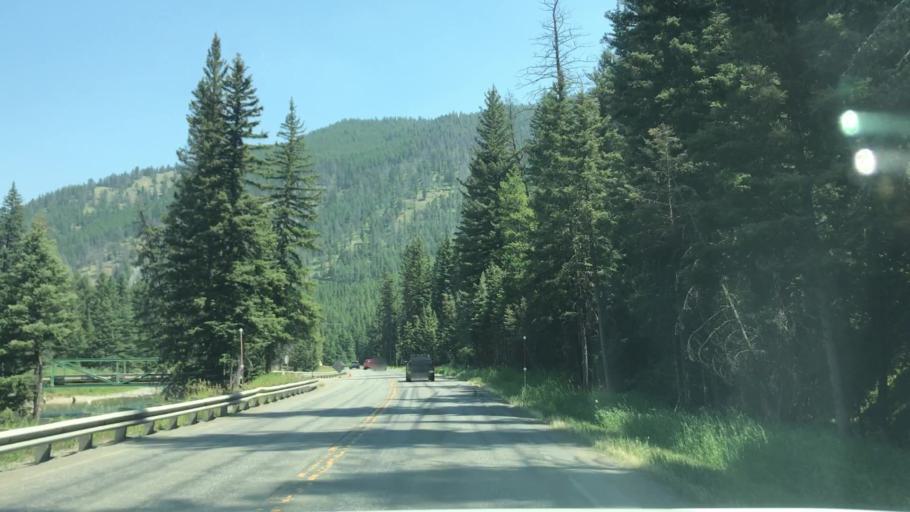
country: US
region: Montana
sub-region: Gallatin County
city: Big Sky
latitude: 45.2979
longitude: -111.2044
